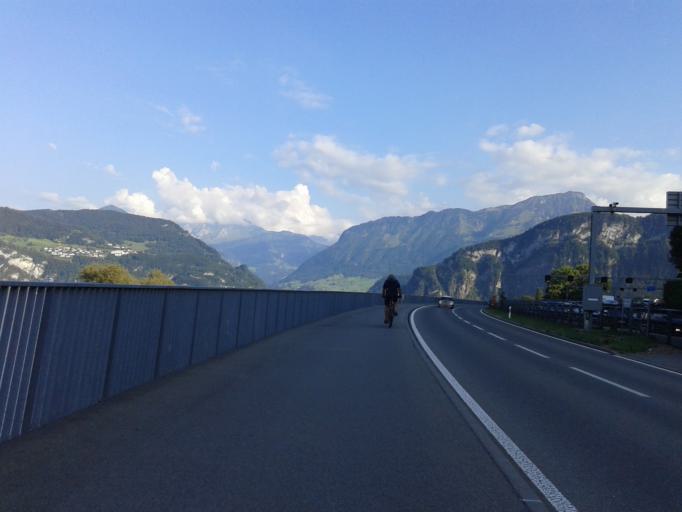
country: CH
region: Lucerne
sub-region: Lucerne-Land District
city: Horw
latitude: 47.0019
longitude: 8.3104
